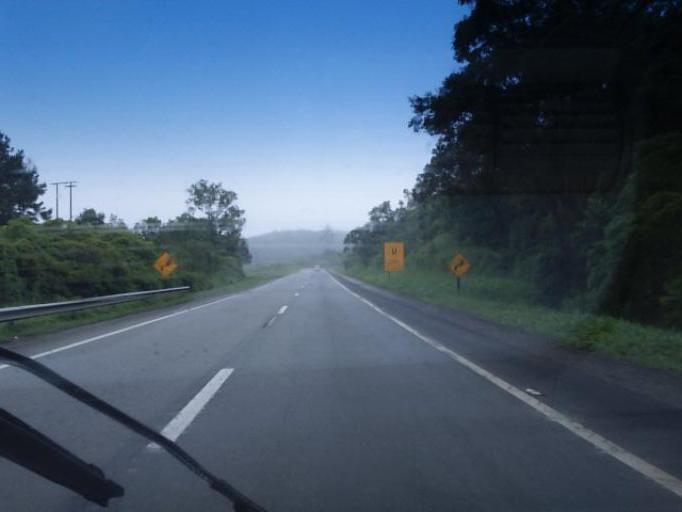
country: BR
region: Parana
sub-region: Campina Grande Do Sul
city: Campina Grande do Sul
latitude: -25.1085
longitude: -48.7915
